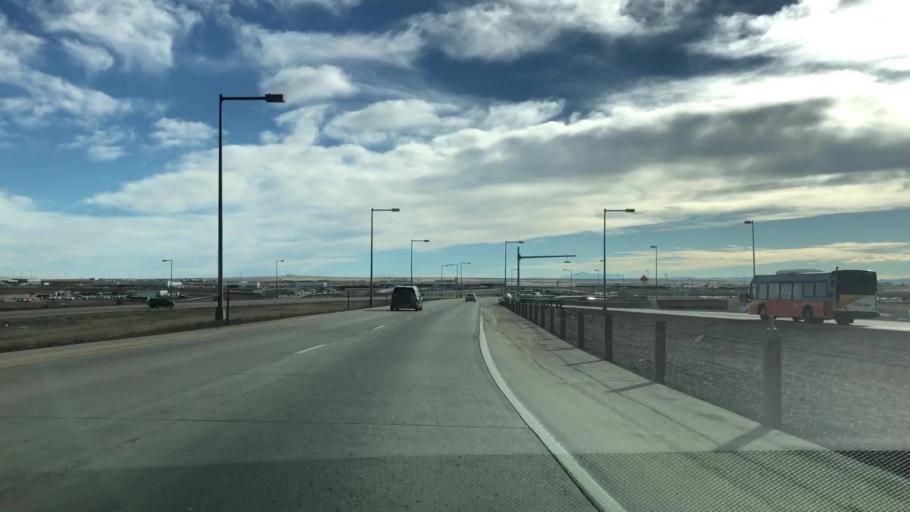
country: US
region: Colorado
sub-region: Weld County
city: Lochbuie
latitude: 39.8444
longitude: -104.6698
